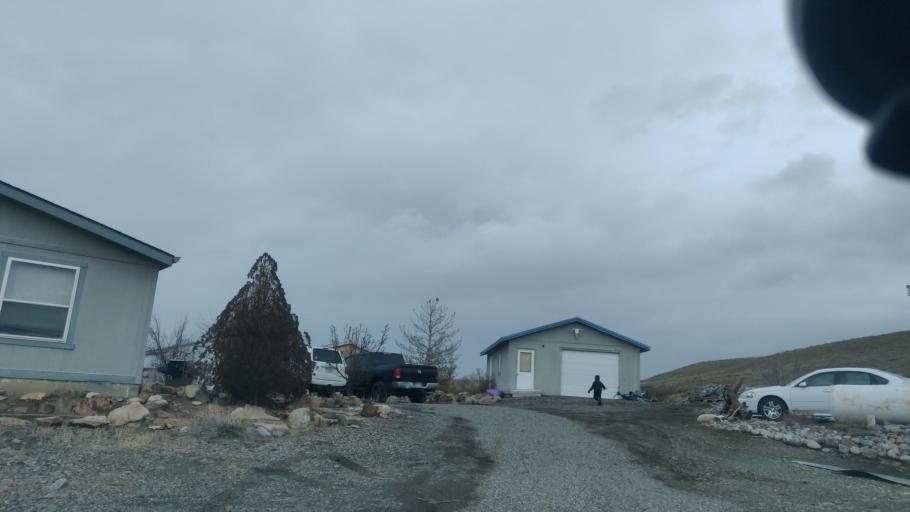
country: US
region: Colorado
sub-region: Mesa County
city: Clifton
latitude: 38.9428
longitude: -108.3964
